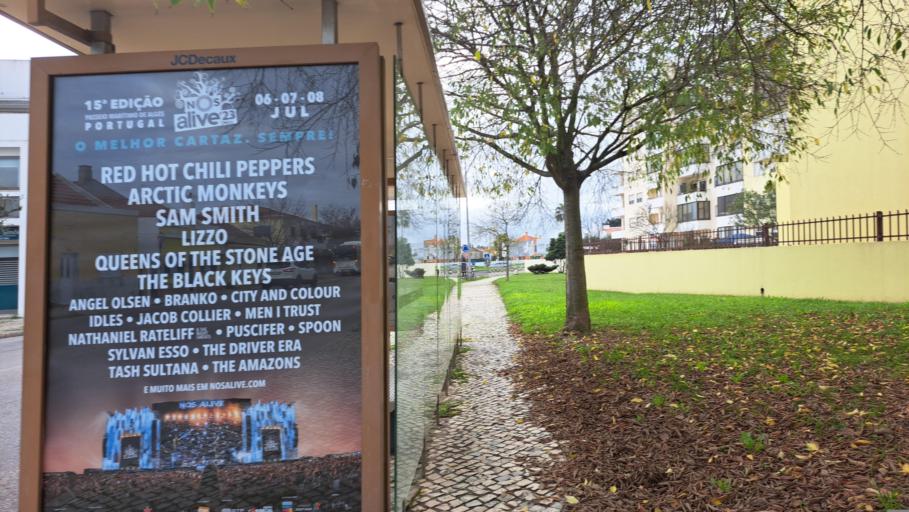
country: PT
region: Setubal
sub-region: Moita
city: Alhos Vedros
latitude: 38.6495
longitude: -9.0467
